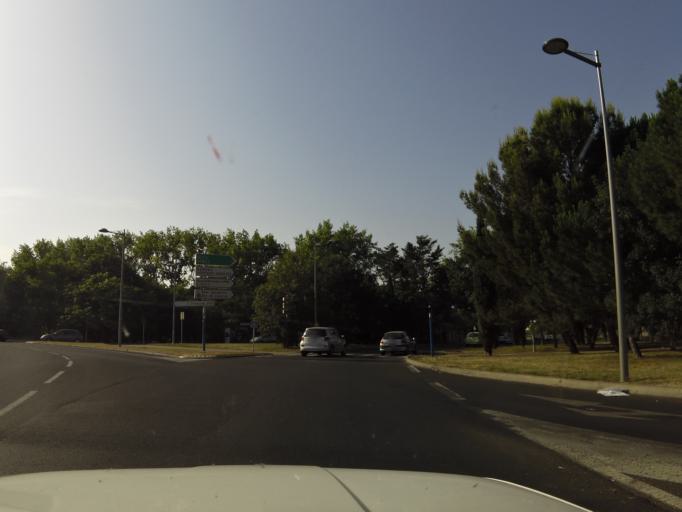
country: FR
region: Languedoc-Roussillon
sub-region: Departement de l'Herault
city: Juvignac
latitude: 43.6314
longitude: 3.8428
